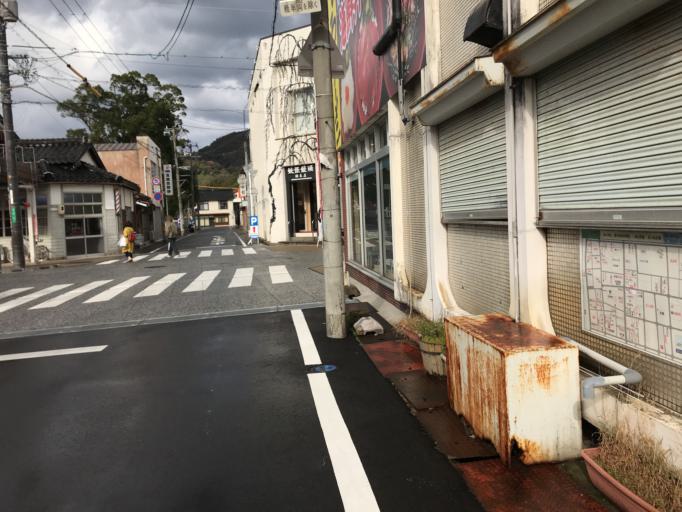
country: JP
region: Shimane
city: Sakaiminato
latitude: 35.5459
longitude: 133.2306
